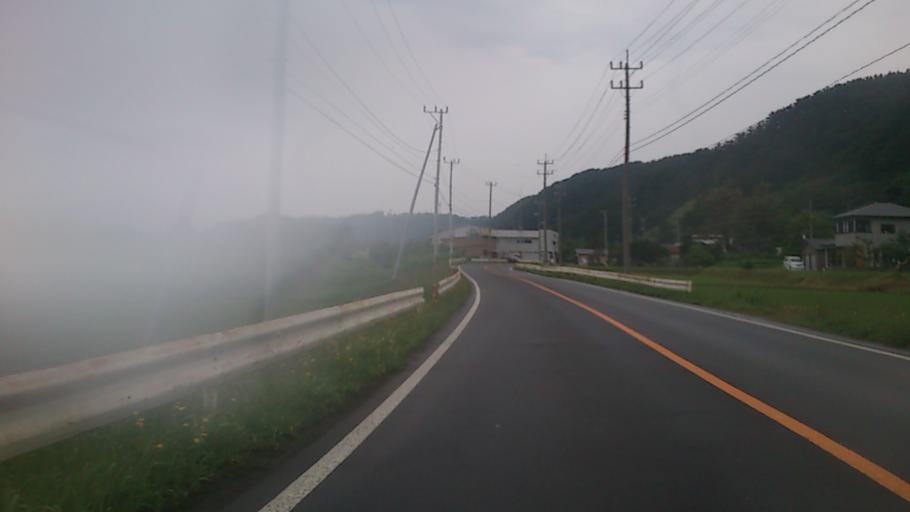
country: JP
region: Akita
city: Noshiromachi
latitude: 40.5450
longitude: 139.9453
